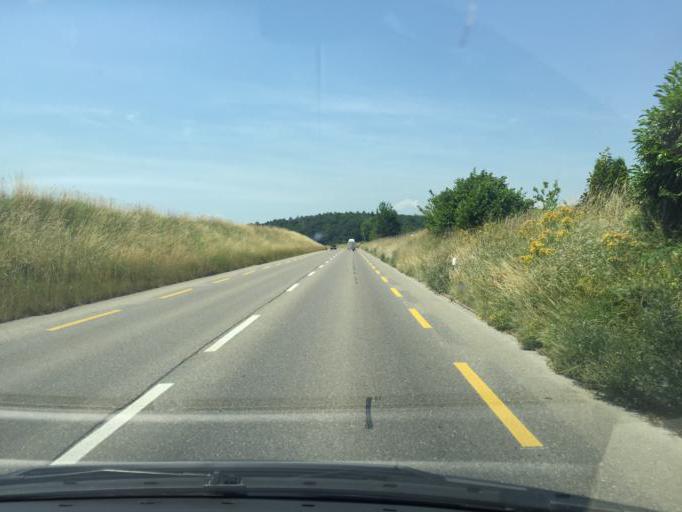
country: CH
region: Schaffhausen
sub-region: Bezirk Stein
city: Ramsen
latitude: 47.6736
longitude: 8.8078
